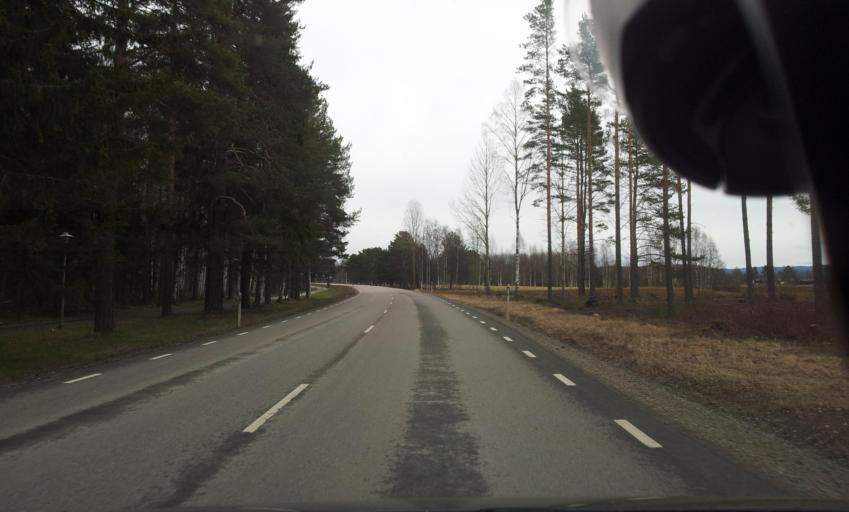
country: SE
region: Gaevleborg
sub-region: Ljusdals Kommun
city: Ljusdal
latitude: 61.8196
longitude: 16.0909
